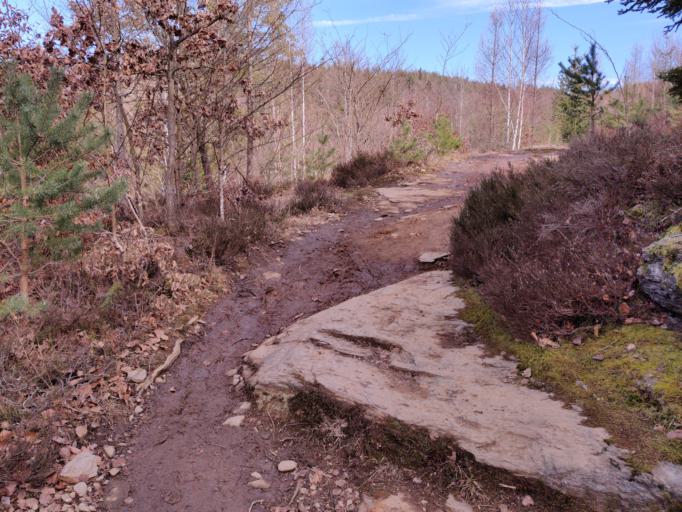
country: AT
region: Carinthia
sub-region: Klagenfurt am Woerthersee
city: Klagenfurt am Woerthersee
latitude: 46.6286
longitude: 14.2471
